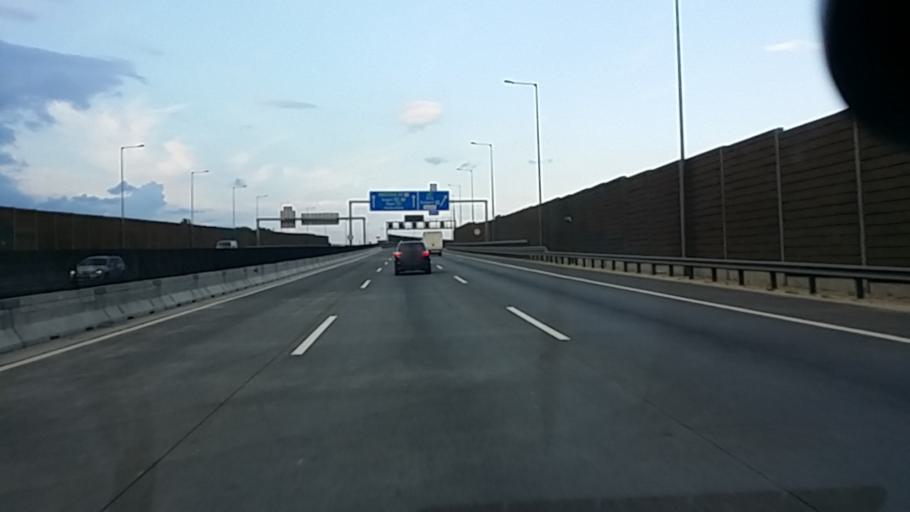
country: HU
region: Pest
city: Halasztelek
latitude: 47.3998
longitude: 19.0011
